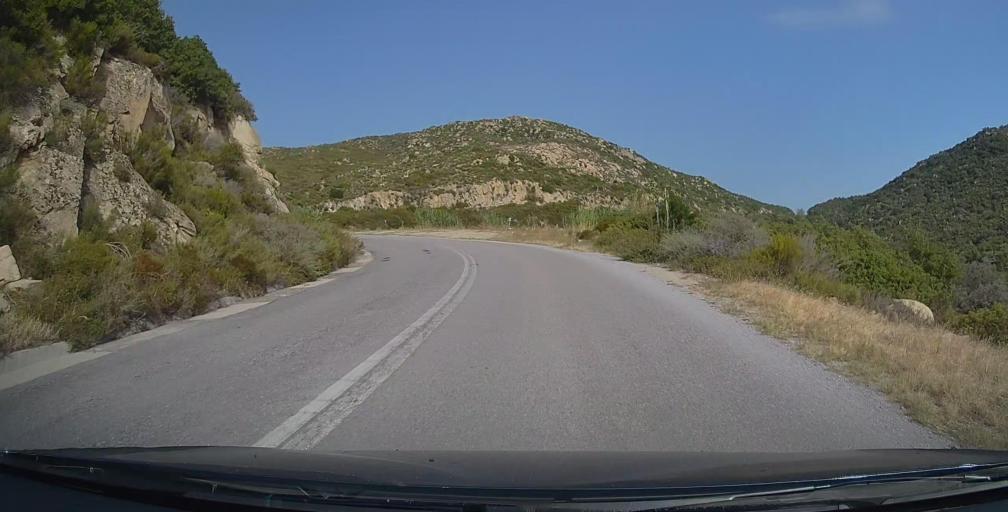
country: GR
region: Central Macedonia
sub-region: Nomos Chalkidikis
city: Sykia
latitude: 39.9970
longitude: 23.9860
